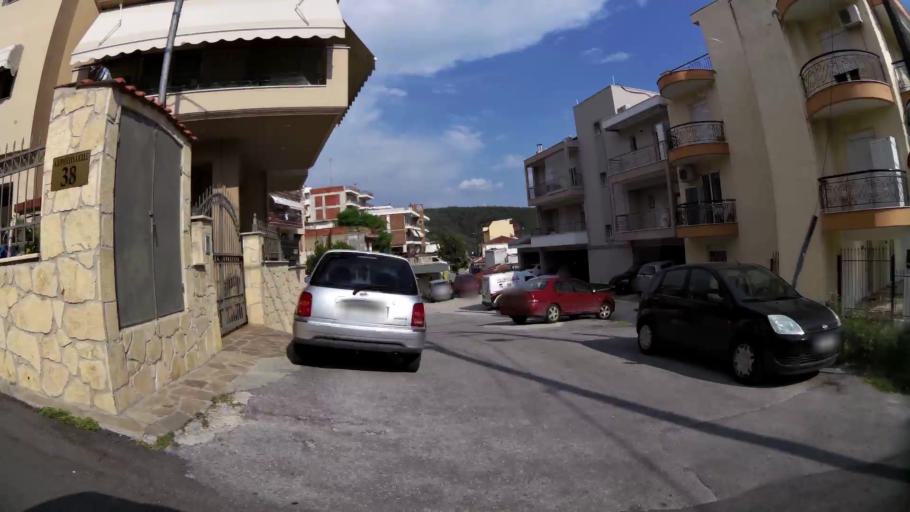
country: GR
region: Central Macedonia
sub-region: Nomos Thessalonikis
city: Sykies
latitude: 40.6594
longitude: 22.9619
